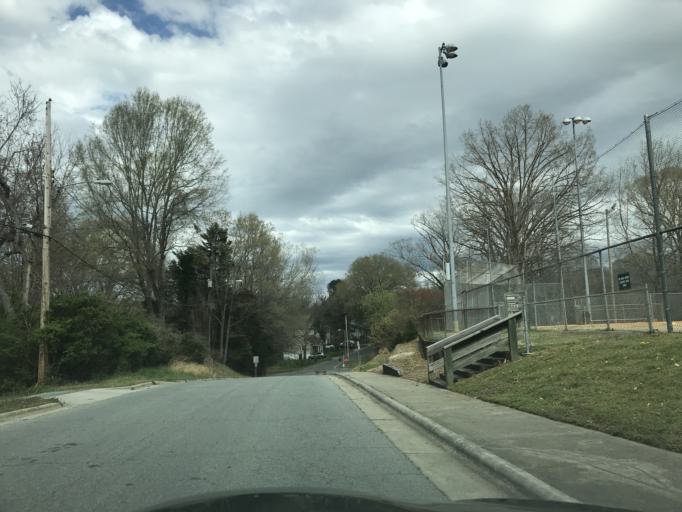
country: US
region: North Carolina
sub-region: Orange County
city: Chapel Hill
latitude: 35.9139
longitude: -79.0641
